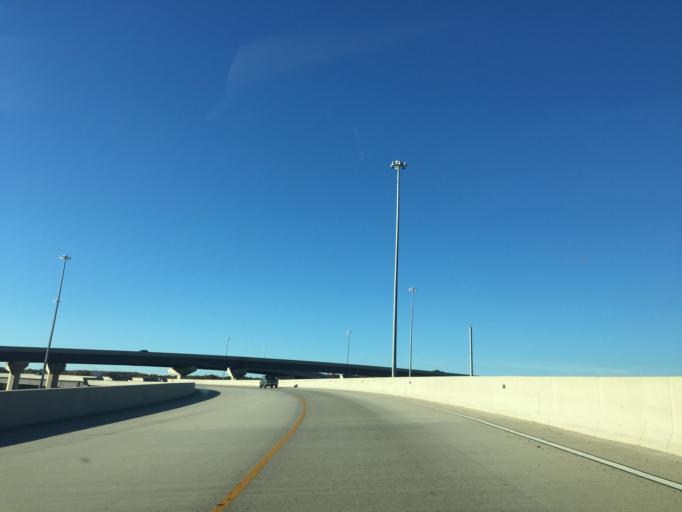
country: US
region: Maryland
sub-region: Baltimore County
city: Rossville
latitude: 39.3501
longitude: -76.4941
